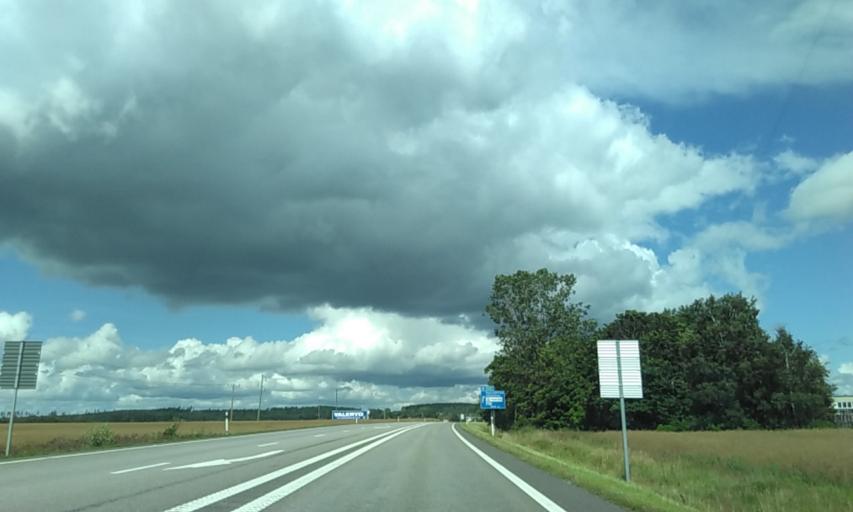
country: SE
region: Vaestra Goetaland
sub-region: Vargarda Kommun
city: Vargarda
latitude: 58.0352
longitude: 12.7885
